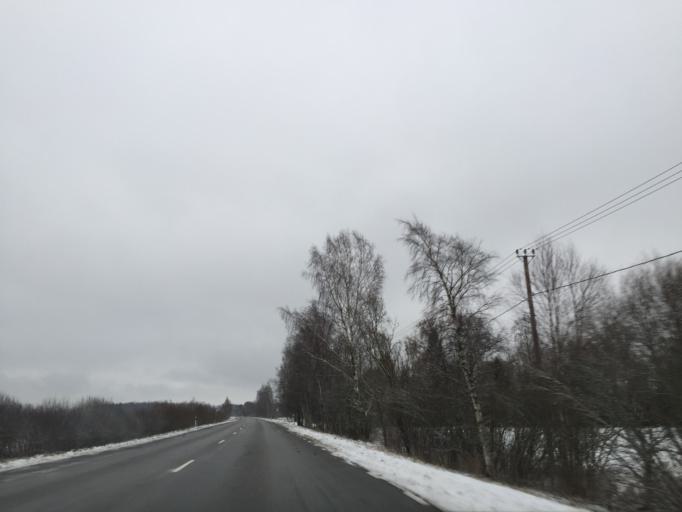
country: EE
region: Laeaene
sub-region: Lihula vald
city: Lihula
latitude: 58.6355
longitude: 23.8644
